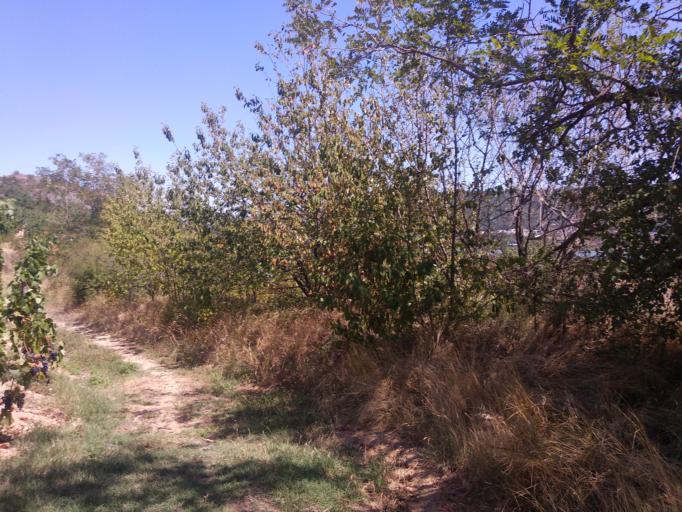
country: FR
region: Rhone-Alpes
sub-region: Departement de l'Ardeche
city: Sarras
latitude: 45.1876
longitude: 4.7937
